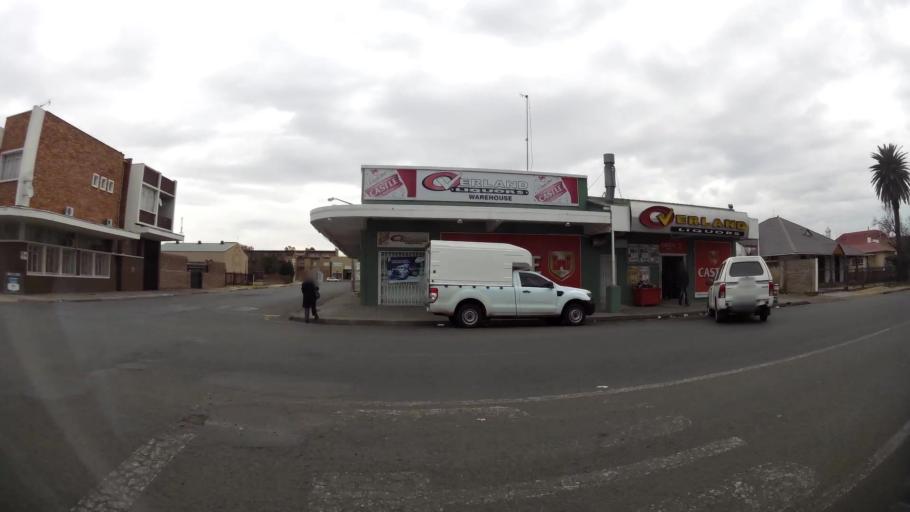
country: ZA
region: Orange Free State
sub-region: Fezile Dabi District Municipality
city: Kroonstad
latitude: -27.6619
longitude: 27.2382
